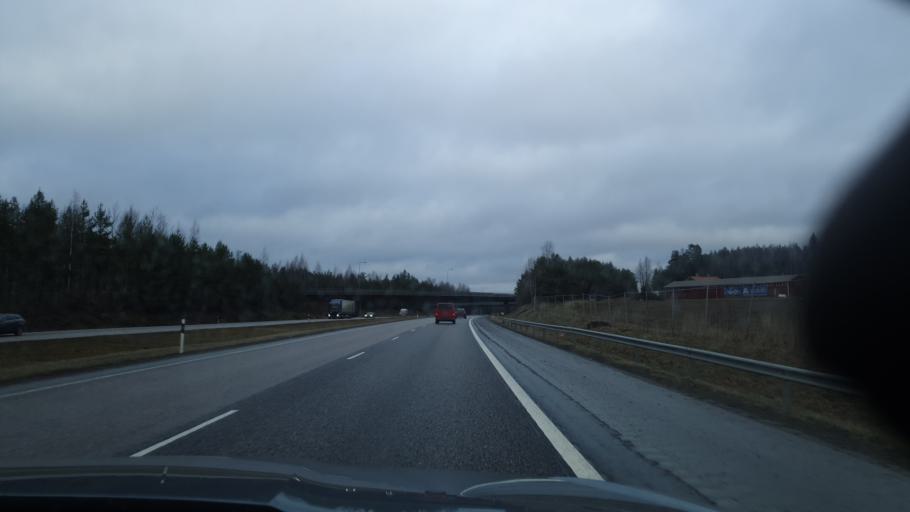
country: FI
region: Uusimaa
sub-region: Helsinki
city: Hyvinge
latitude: 60.5862
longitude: 24.7993
